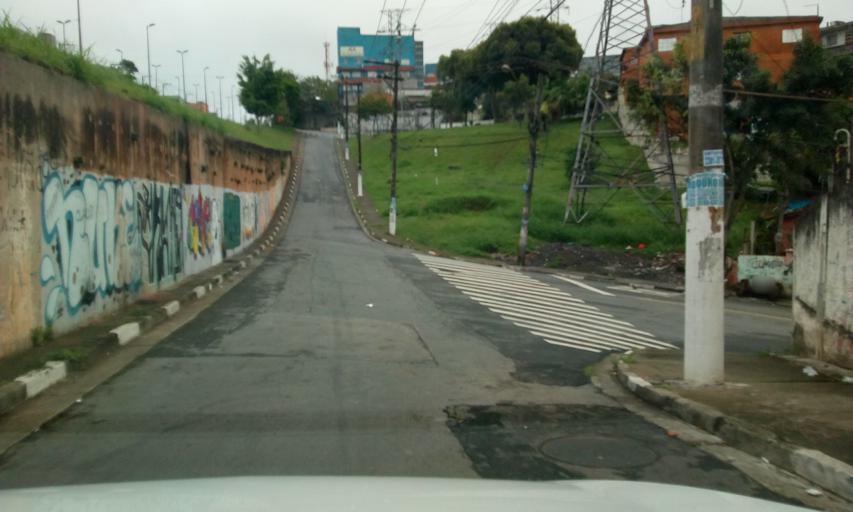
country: BR
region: Sao Paulo
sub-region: Diadema
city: Diadema
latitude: -23.6805
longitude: -46.6265
